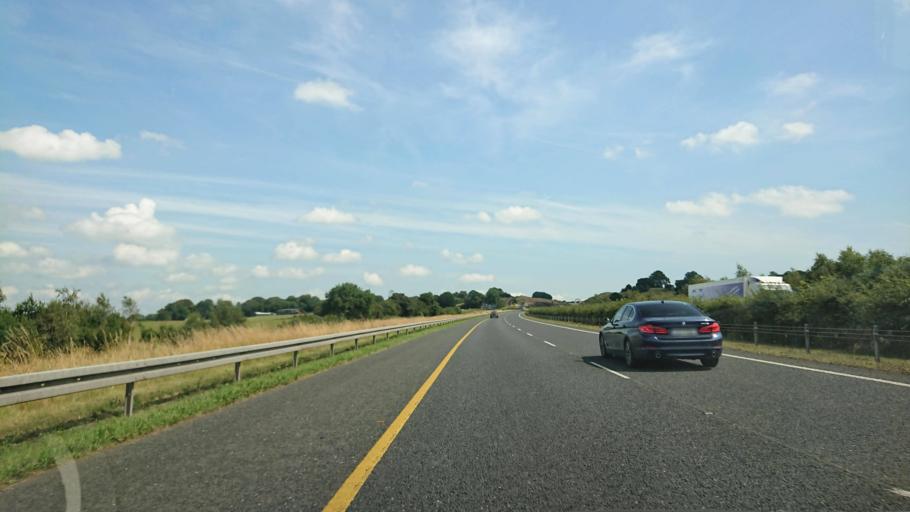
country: IE
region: Leinster
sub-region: An Mhi
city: Enfield
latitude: 53.4098
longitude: -6.7769
